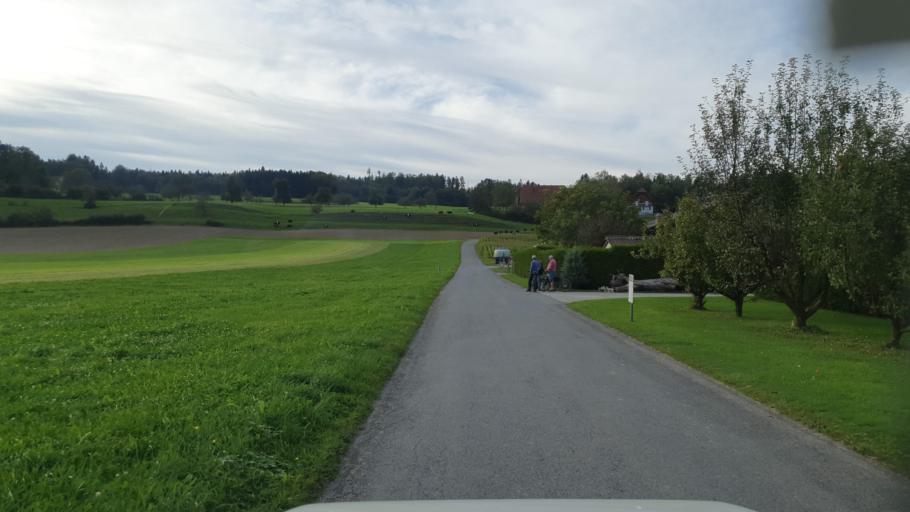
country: CH
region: Lucerne
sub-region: Hochdorf District
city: Hohenrain
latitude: 47.1773
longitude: 8.3531
